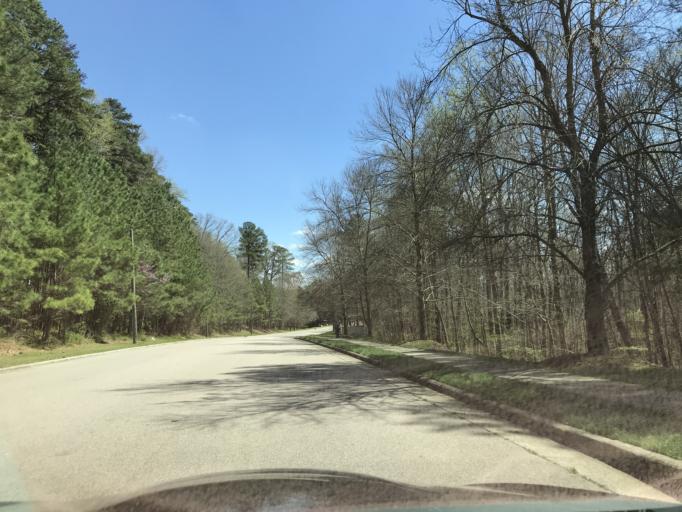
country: US
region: North Carolina
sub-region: Wake County
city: Cary
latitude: 35.8772
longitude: -78.7249
